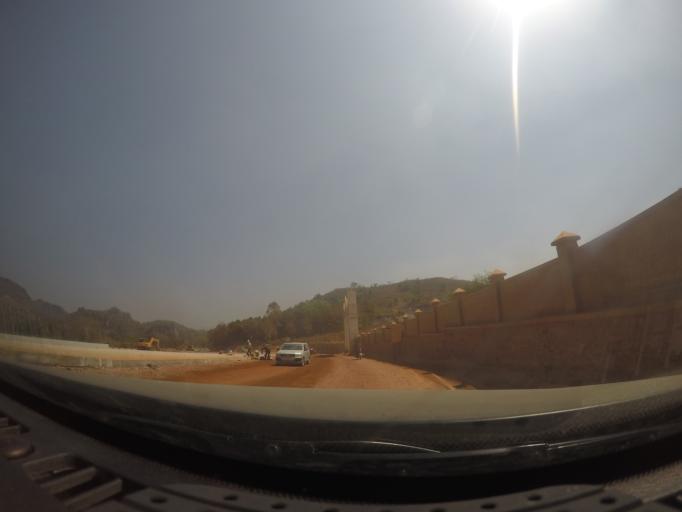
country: MM
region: Shan
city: Taunggyi
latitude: 20.7760
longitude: 97.1347
